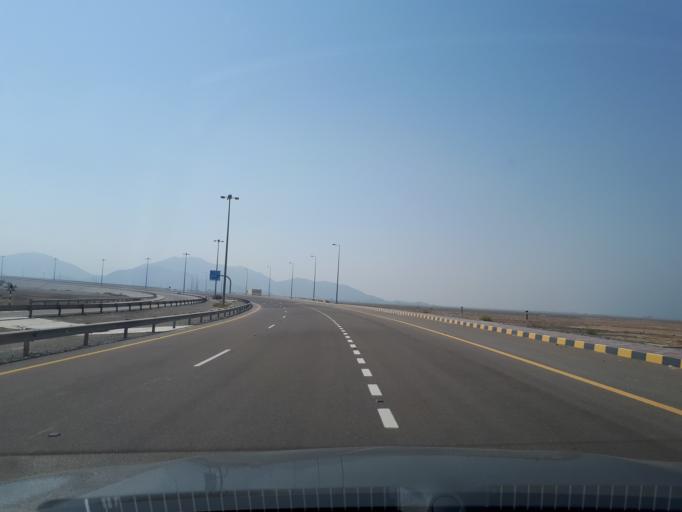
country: AE
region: Al Fujayrah
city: Al Fujayrah
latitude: 24.9509
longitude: 56.3795
